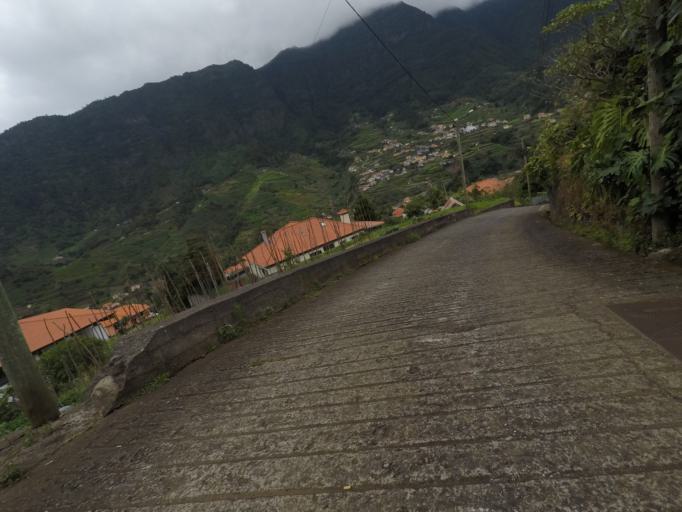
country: PT
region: Madeira
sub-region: Sao Vicente
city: Sao Vicente
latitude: 32.7886
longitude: -17.0386
